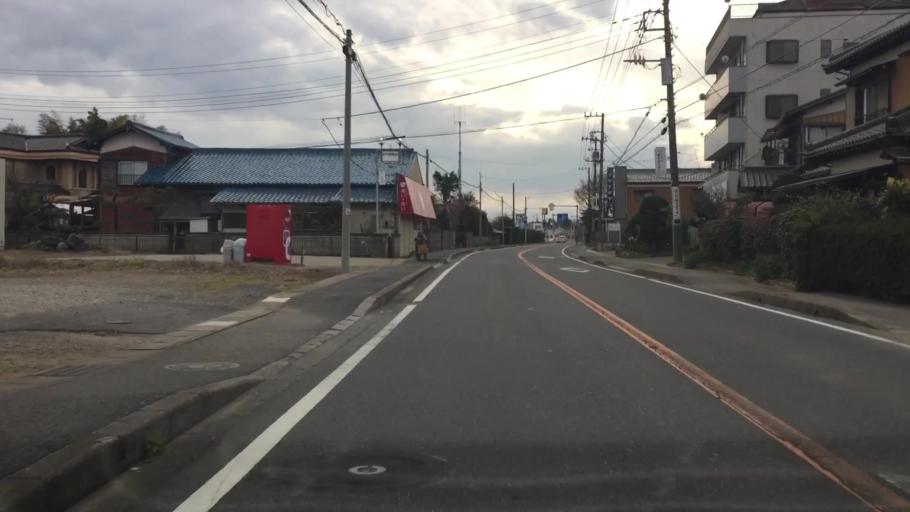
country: JP
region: Chiba
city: Shiroi
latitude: 35.7868
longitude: 140.0498
